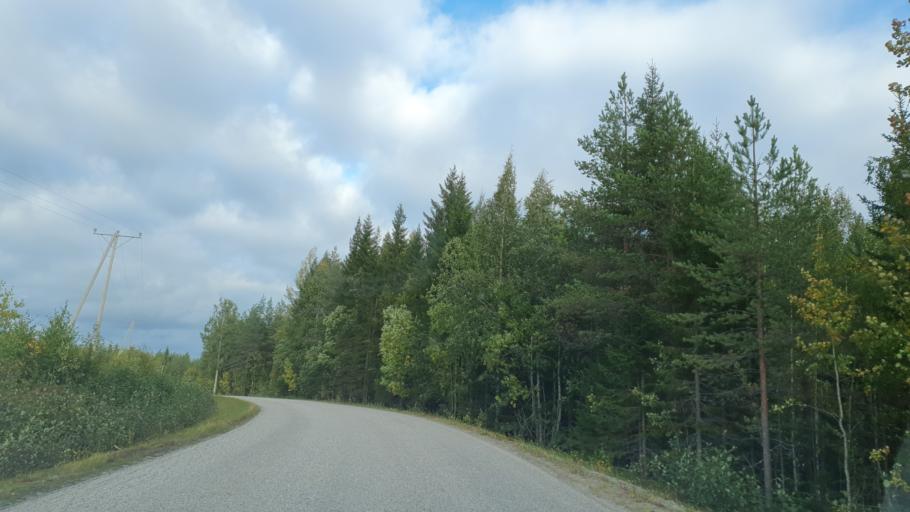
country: FI
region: Kainuu
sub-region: Kehys-Kainuu
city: Kuhmo
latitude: 63.9249
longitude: 30.0161
